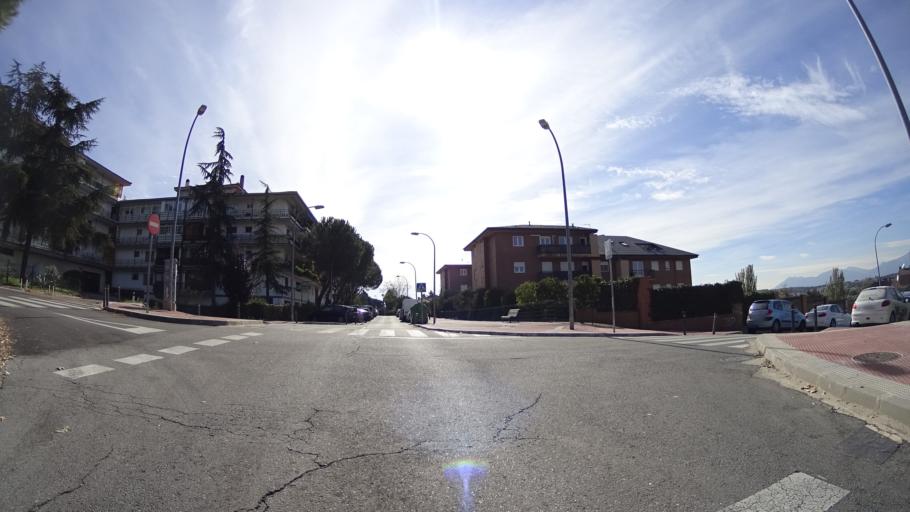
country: ES
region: Madrid
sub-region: Provincia de Madrid
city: Collado-Villalba
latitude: 40.6183
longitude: -4.0138
